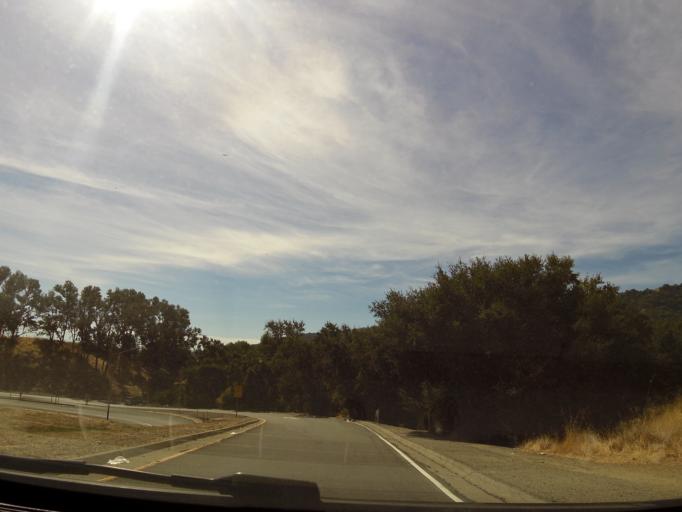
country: US
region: California
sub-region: Alameda County
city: Pleasanton
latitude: 37.6405
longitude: -121.8859
